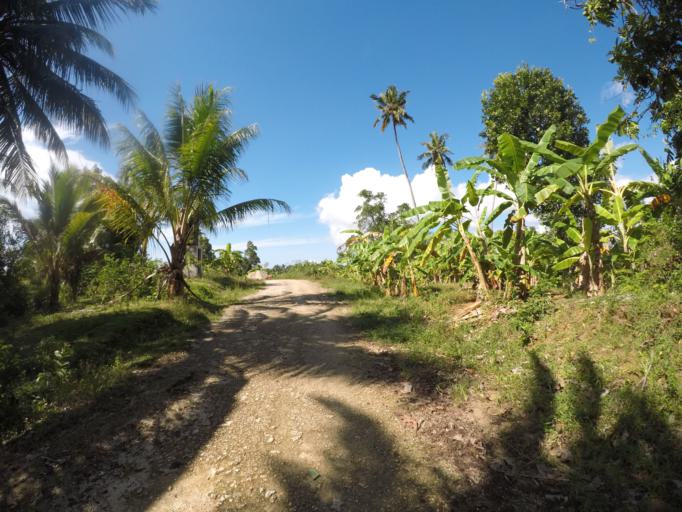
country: TZ
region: Pemba South
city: Mtambile
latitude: -5.3460
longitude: 39.6903
